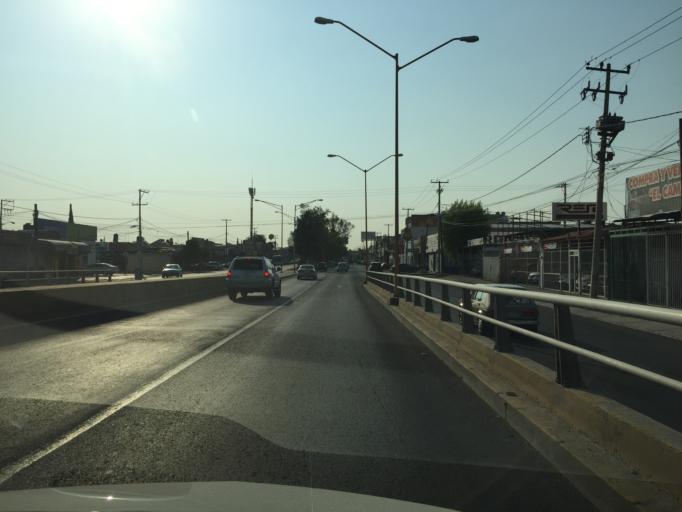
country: MX
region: Aguascalientes
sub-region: Aguascalientes
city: Aguascalientes
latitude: 21.8589
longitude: -102.3121
